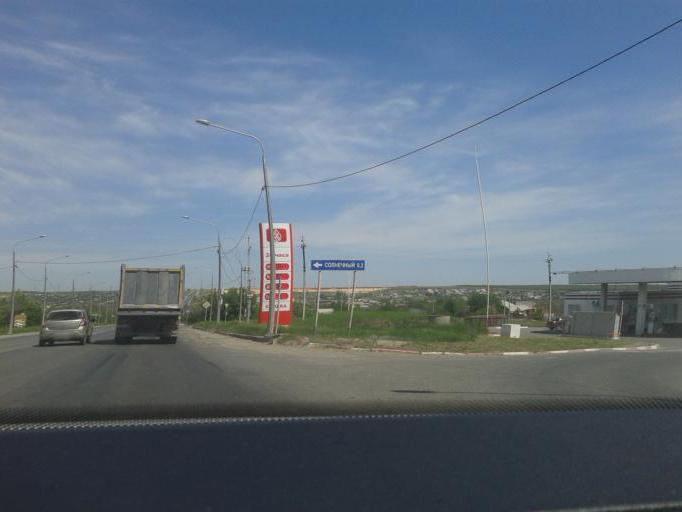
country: RU
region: Volgograd
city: Gorodishche
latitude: 48.7879
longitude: 44.5205
